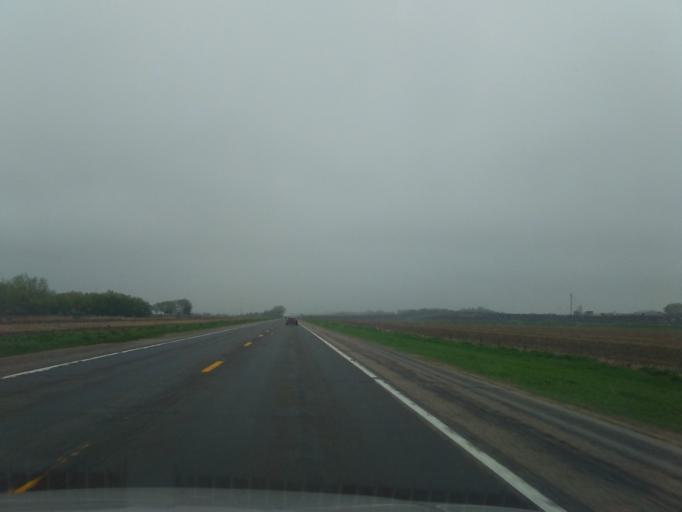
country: US
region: Nebraska
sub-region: Cuming County
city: Wisner
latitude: 41.9422
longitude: -96.8374
